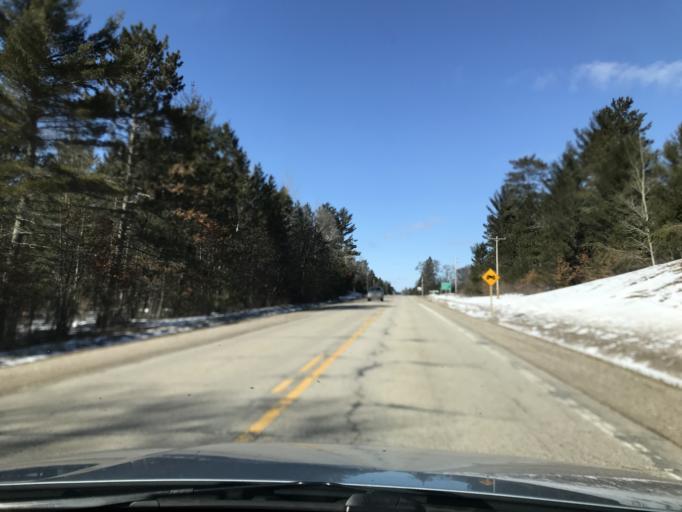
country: US
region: Wisconsin
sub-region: Marinette County
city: Niagara
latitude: 45.3969
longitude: -88.0994
